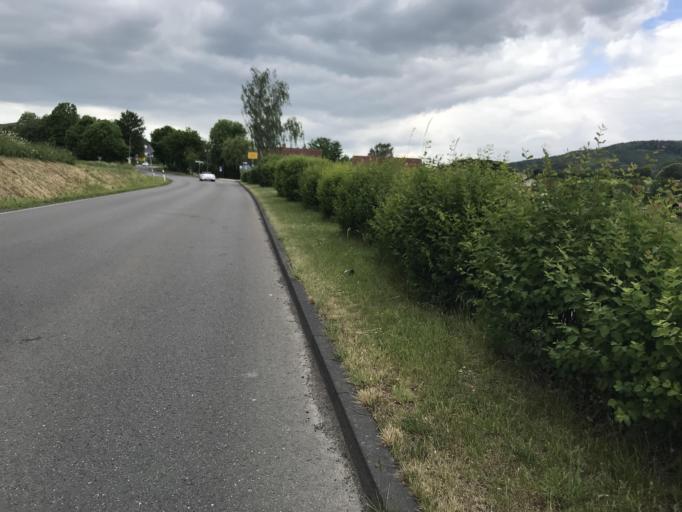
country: DE
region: Hesse
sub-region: Regierungsbezirk Kassel
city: Baunatal
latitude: 51.2798
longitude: 9.3595
